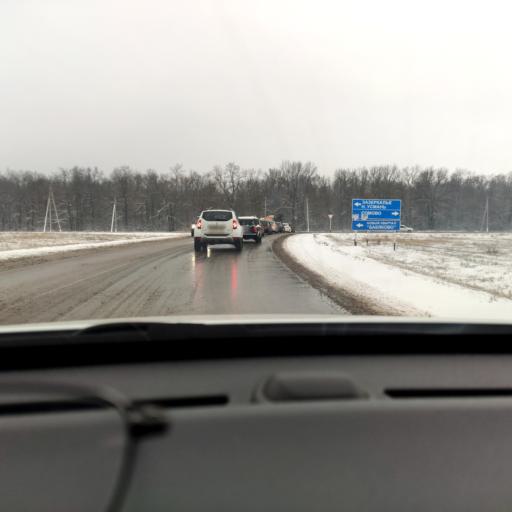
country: RU
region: Voronezj
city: Somovo
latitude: 51.6943
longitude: 39.3881
